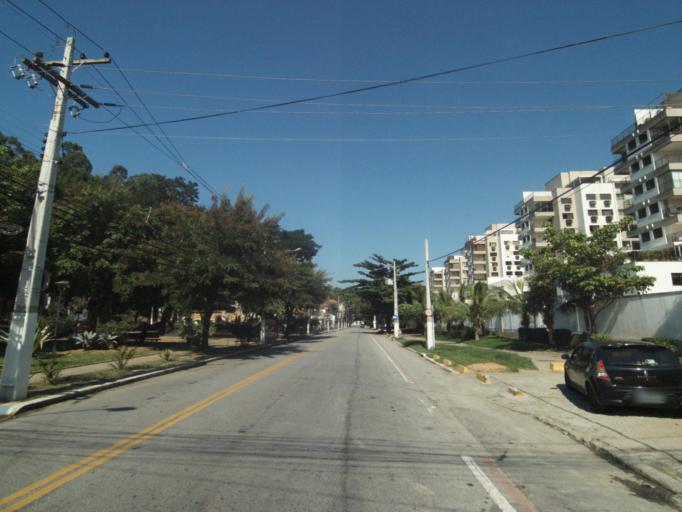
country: BR
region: Rio de Janeiro
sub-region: Niteroi
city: Niteroi
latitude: -22.9008
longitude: -43.1320
